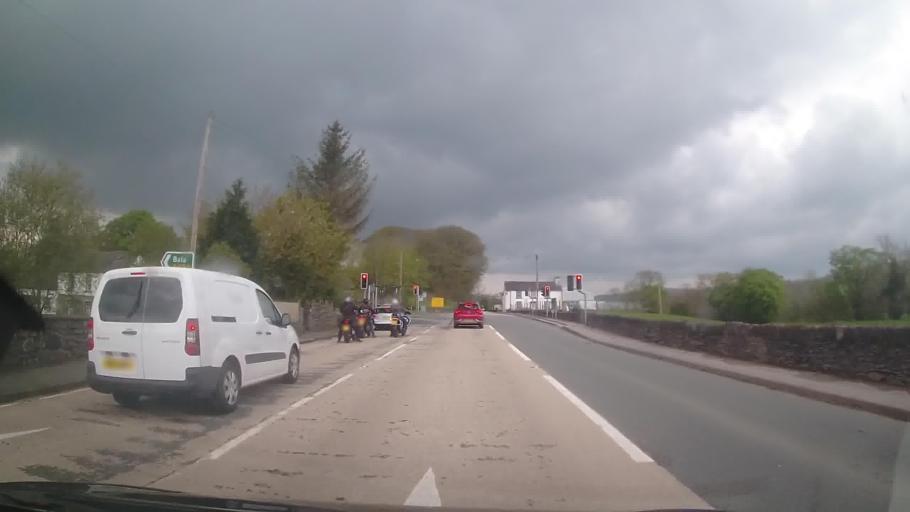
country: GB
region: Wales
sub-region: Denbighshire
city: Corwen
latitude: 52.9797
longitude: -3.4291
